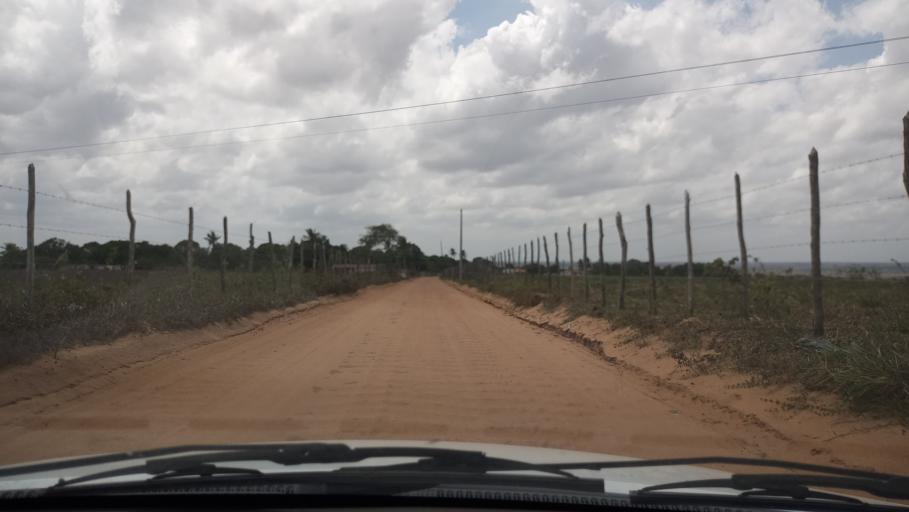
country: BR
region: Rio Grande do Norte
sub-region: Montanhas
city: Montanhas
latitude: -6.3608
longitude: -35.3347
